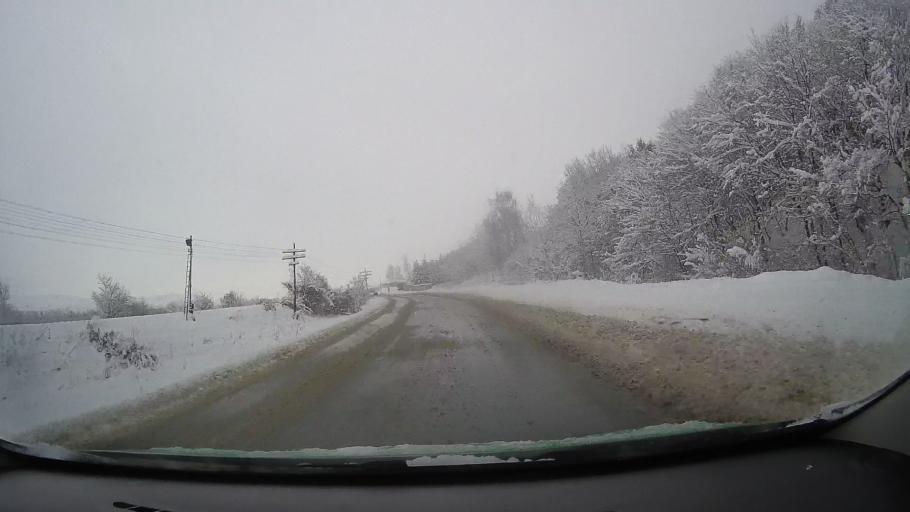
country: RO
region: Sibiu
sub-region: Comuna Orlat
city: Orlat
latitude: 45.7577
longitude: 23.9443
